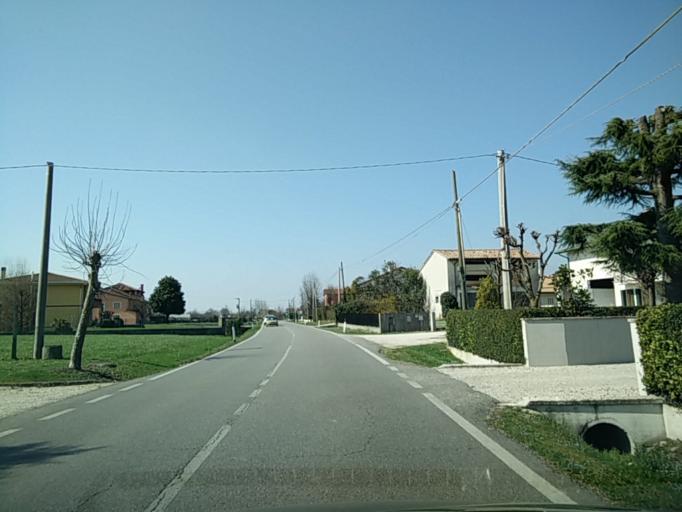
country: IT
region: Veneto
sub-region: Provincia di Treviso
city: Valla
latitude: 45.7032
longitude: 11.9196
